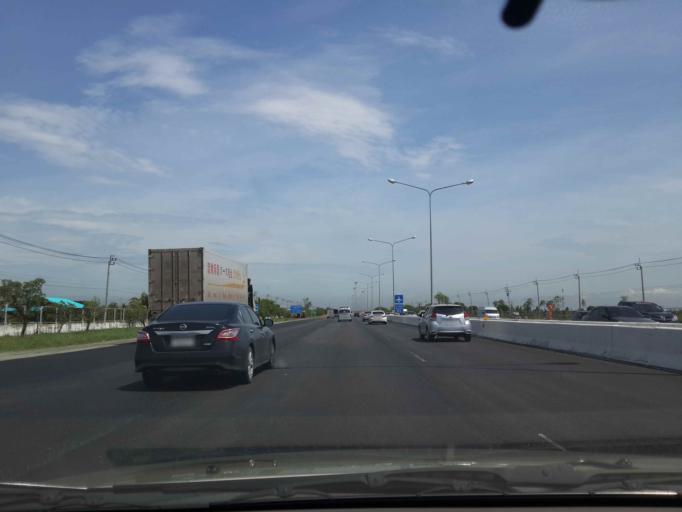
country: TH
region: Samut Prakan
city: Ban Khlong Bang Sao Thong
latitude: 13.6427
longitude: 100.8862
